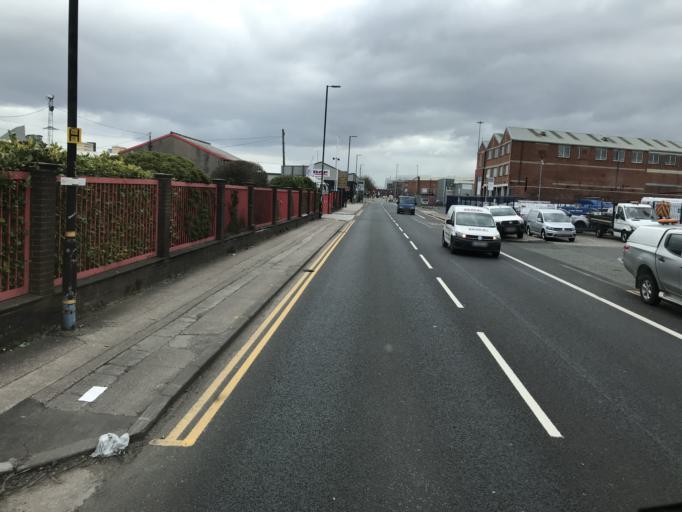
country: GB
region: England
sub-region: Trafford
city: Trafford Park
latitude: 53.4683
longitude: -2.3092
